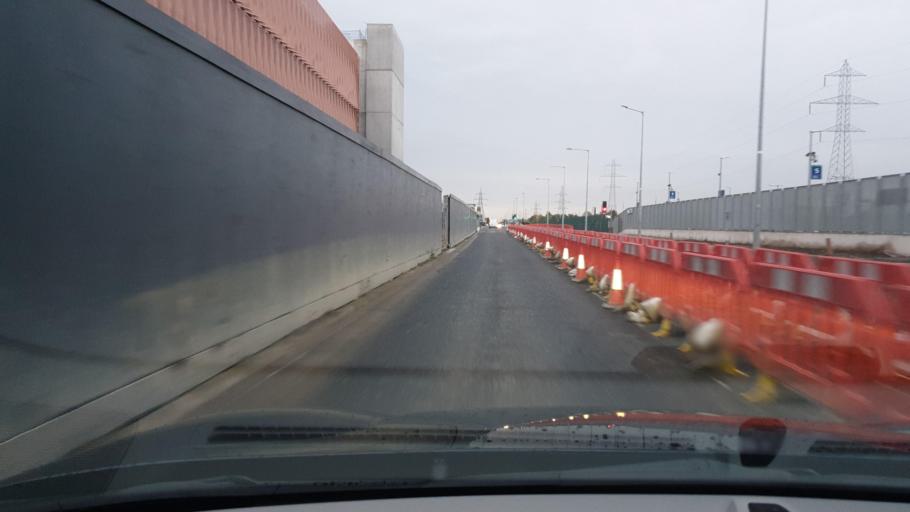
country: IE
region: Leinster
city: Lucan
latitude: 53.3363
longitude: -6.4693
